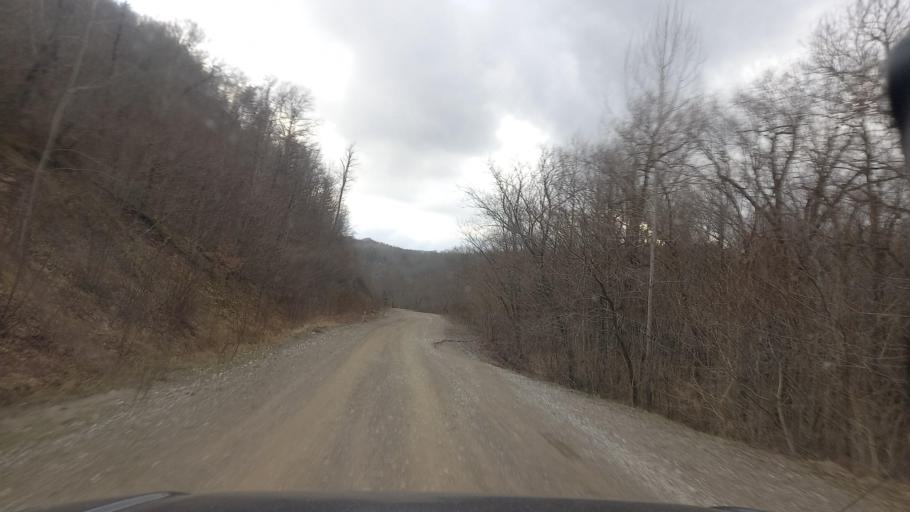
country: RU
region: Krasnodarskiy
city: Dzhubga
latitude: 44.5334
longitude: 38.7773
